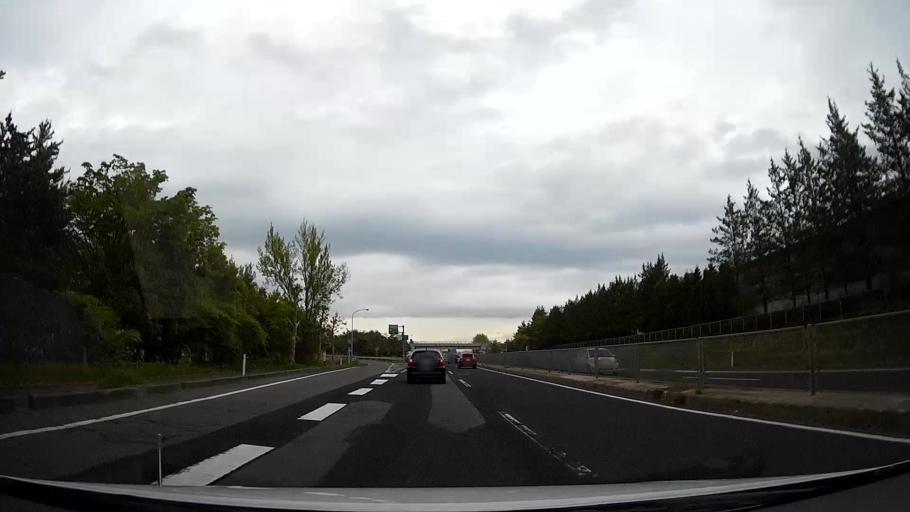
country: JP
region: Yamagata
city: Yamagata-shi
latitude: 38.2913
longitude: 140.3606
